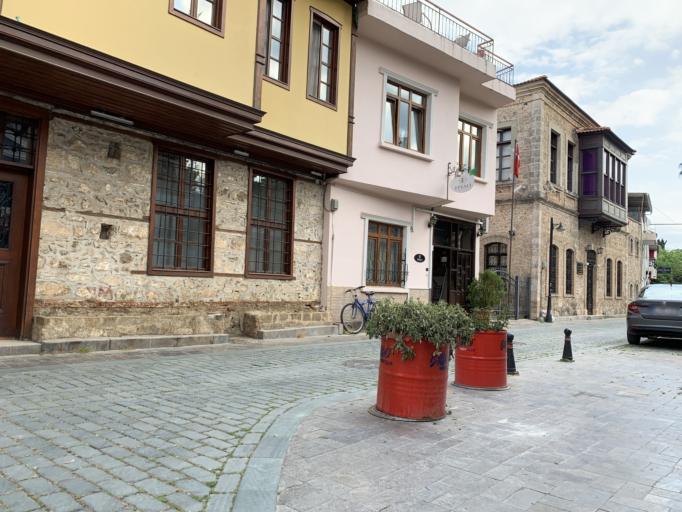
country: TR
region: Antalya
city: Antalya
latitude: 36.8818
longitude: 30.7060
